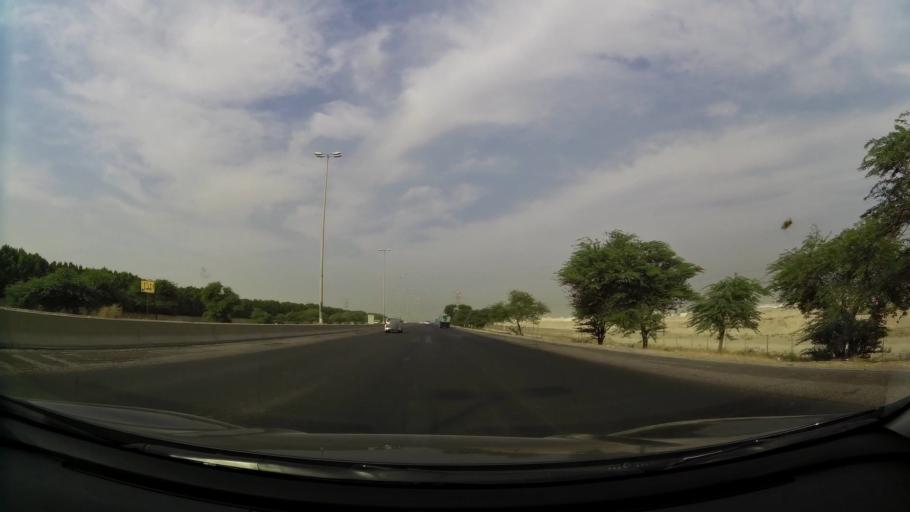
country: KW
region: Muhafazat al Jahra'
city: Al Jahra'
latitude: 29.2917
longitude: 47.7562
